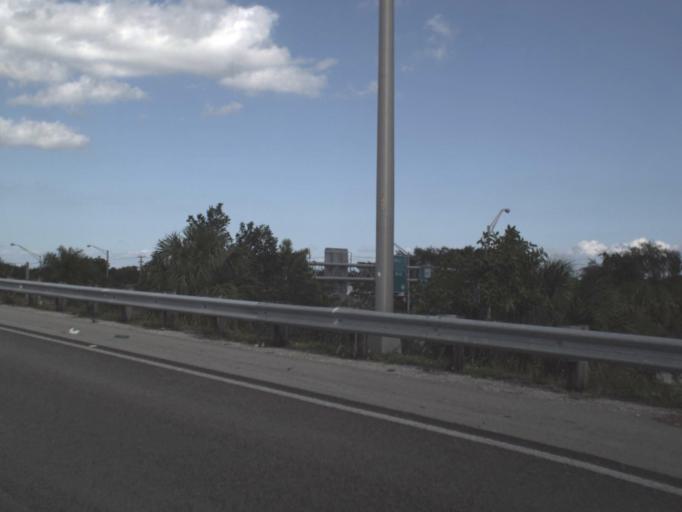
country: US
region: Florida
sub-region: Broward County
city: Pembroke Pines
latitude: 26.0087
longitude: -80.2134
